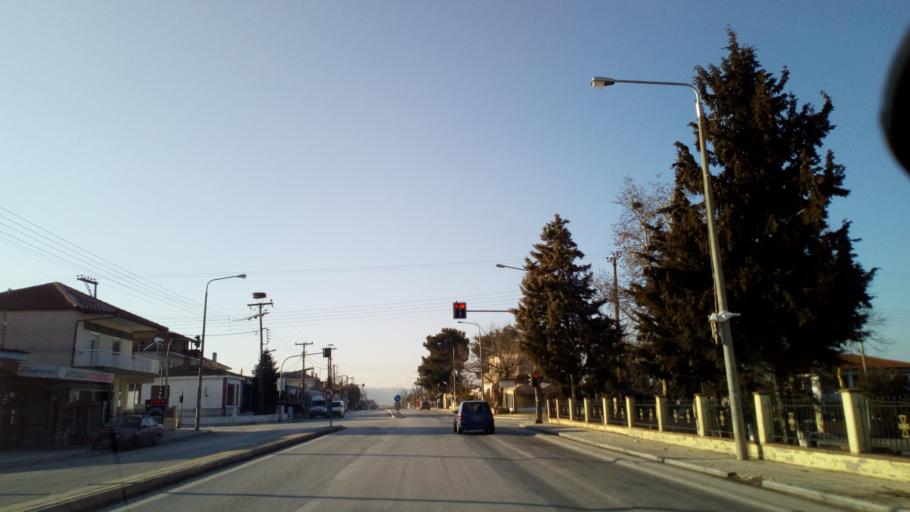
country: GR
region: Central Macedonia
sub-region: Nomos Thessalonikis
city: Agios Vasileios
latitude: 40.6638
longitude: 23.1165
